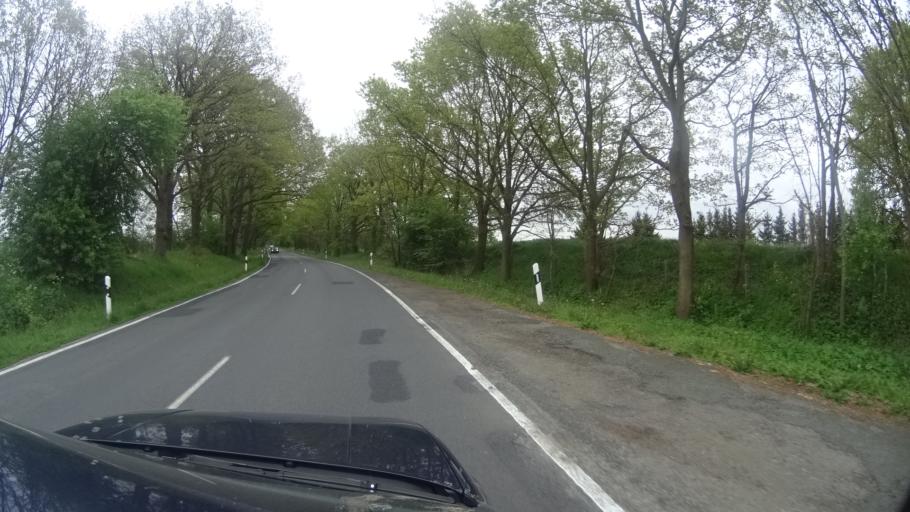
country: DE
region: Mecklenburg-Vorpommern
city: Ostseebad Dierhagen
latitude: 54.2593
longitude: 12.3568
